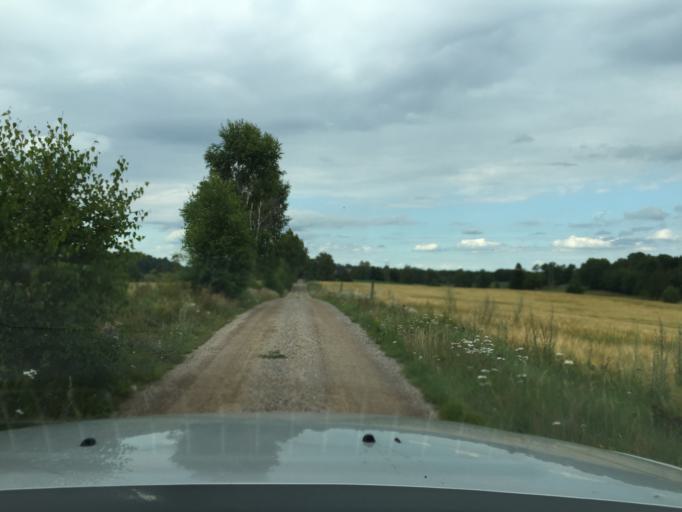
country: SE
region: Skane
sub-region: Hassleholms Kommun
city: Sosdala
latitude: 56.0485
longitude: 13.6896
